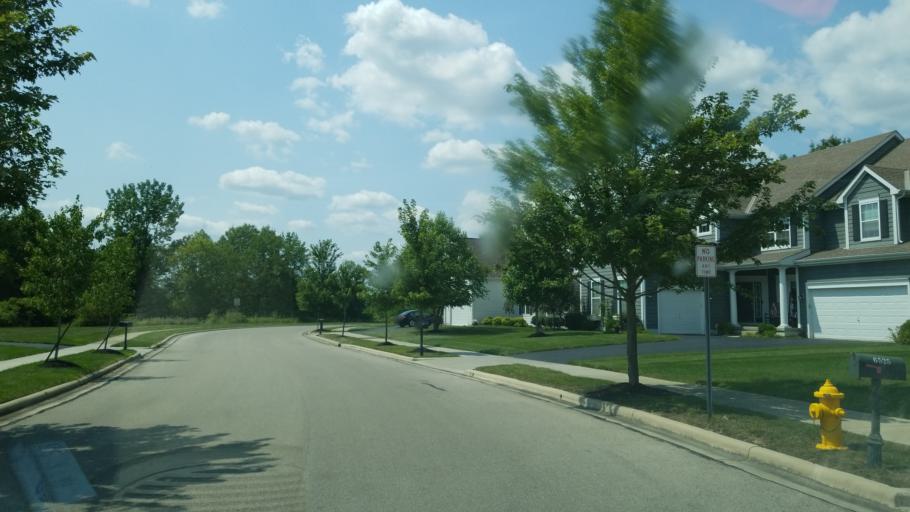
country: US
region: Ohio
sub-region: Delaware County
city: Powell
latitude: 40.2134
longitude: -83.1202
